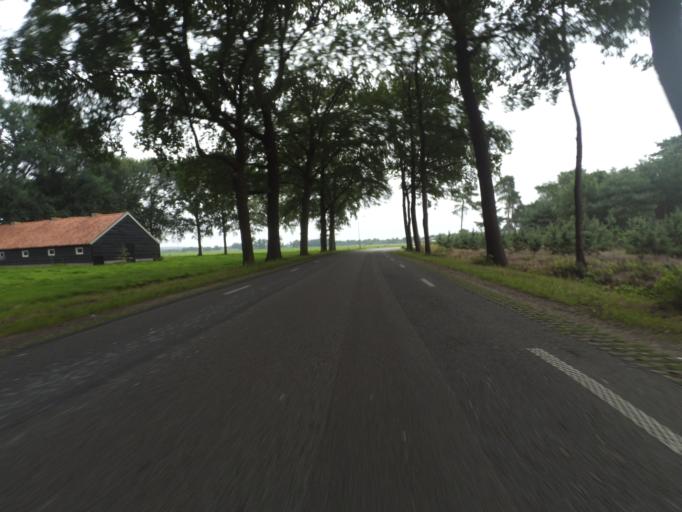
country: NL
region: Gelderland
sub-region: Gemeente Barneveld
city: Kootwijkerbroek
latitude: 52.1523
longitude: 5.6464
